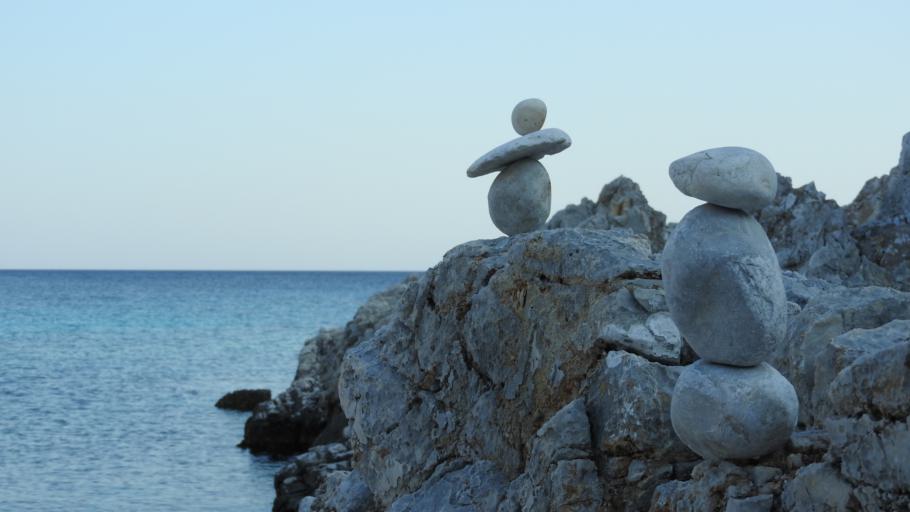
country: GR
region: Central Greece
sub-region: Nomos Evvoias
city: Skyros
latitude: 38.8346
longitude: 24.3665
